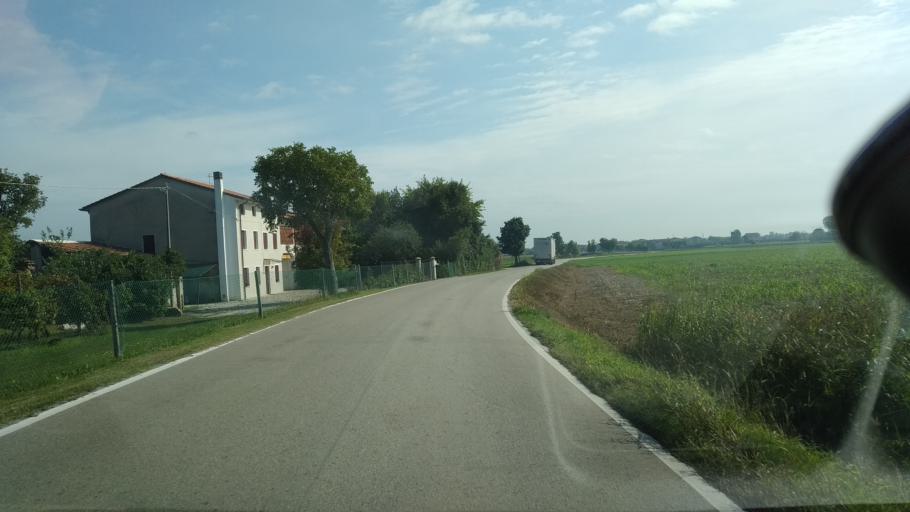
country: IT
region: Veneto
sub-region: Provincia di Vicenza
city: Mason Vicentino
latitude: 45.6975
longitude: 11.5900
